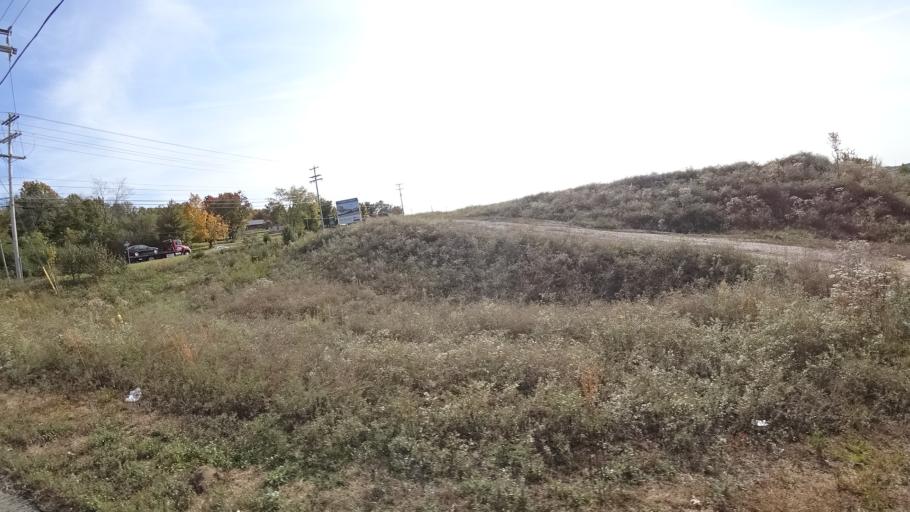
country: US
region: Tennessee
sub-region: Knox County
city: Farragut
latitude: 35.9313
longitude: -84.1474
